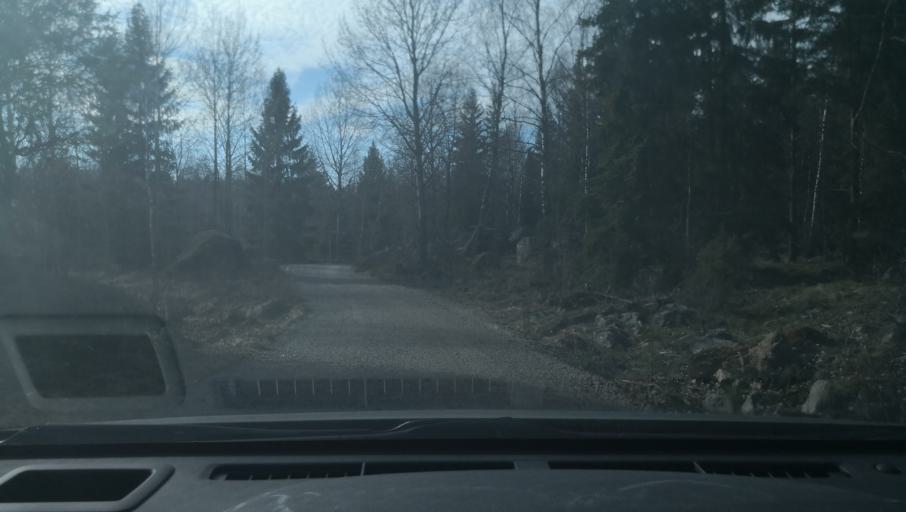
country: SE
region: Uppsala
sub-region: Heby Kommun
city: Heby
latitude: 59.8422
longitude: 16.8544
